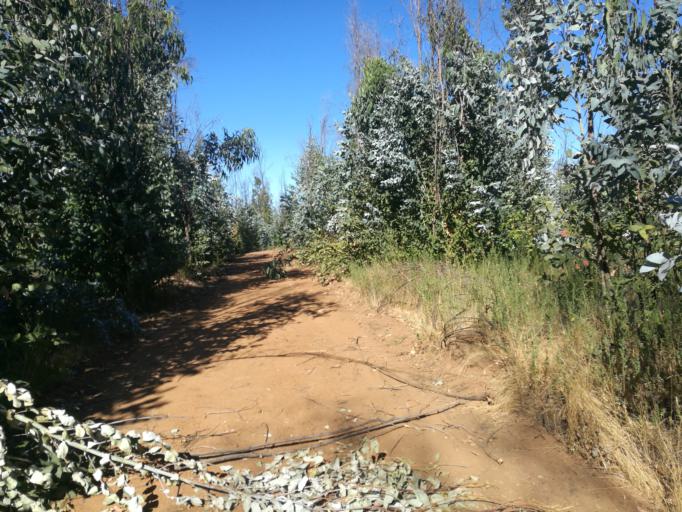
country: CL
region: Valparaiso
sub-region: Provincia de Valparaiso
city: Valparaiso
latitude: -33.0698
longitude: -71.6486
